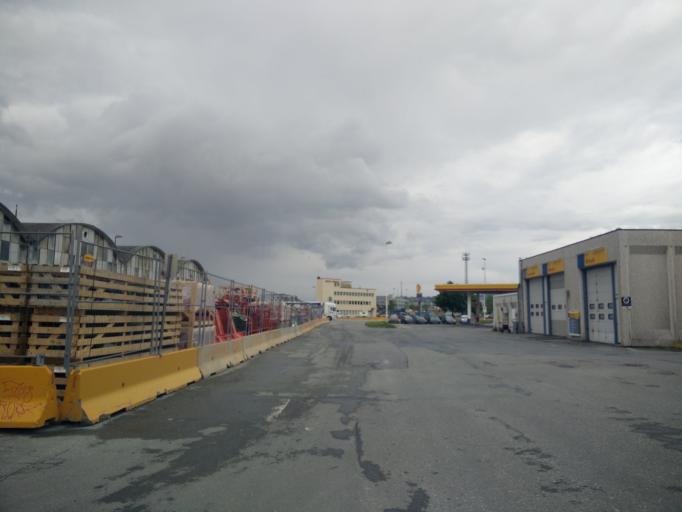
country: NO
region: Sor-Trondelag
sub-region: Trondheim
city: Trondheim
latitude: 63.4407
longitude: 10.4093
